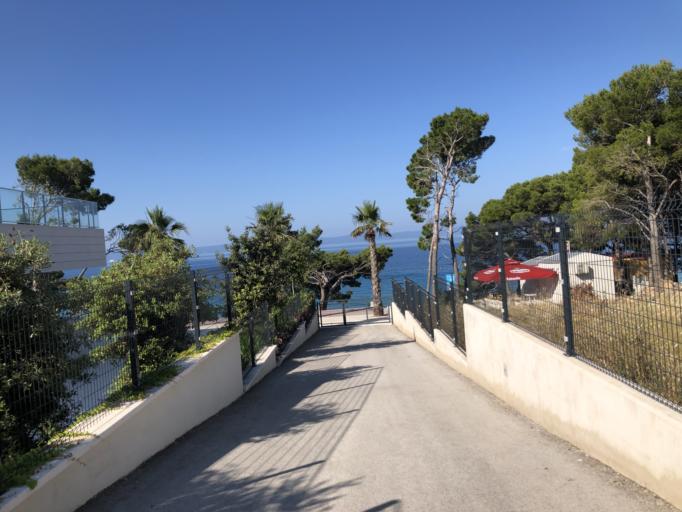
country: HR
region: Splitsko-Dalmatinska
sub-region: Grad Makarska
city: Makarska
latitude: 43.3071
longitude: 17.0013
